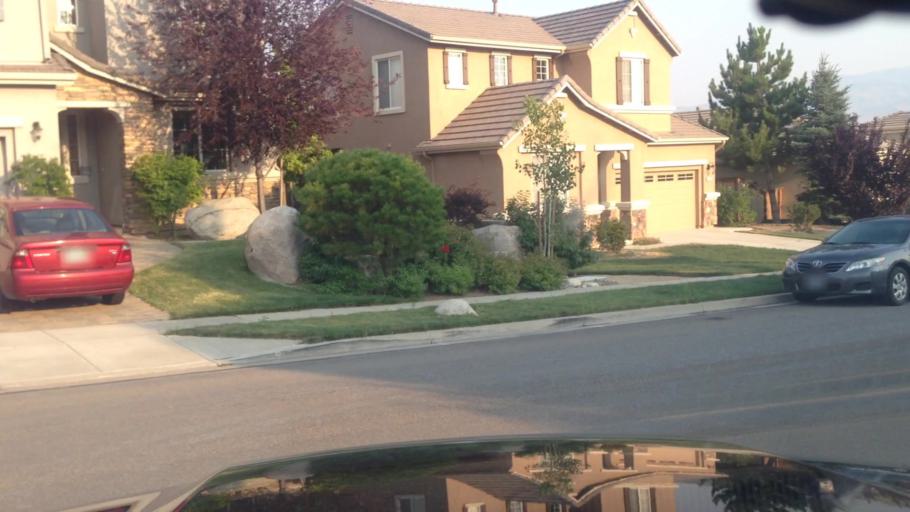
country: US
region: Nevada
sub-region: Washoe County
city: Mogul
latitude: 39.5396
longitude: -119.9157
